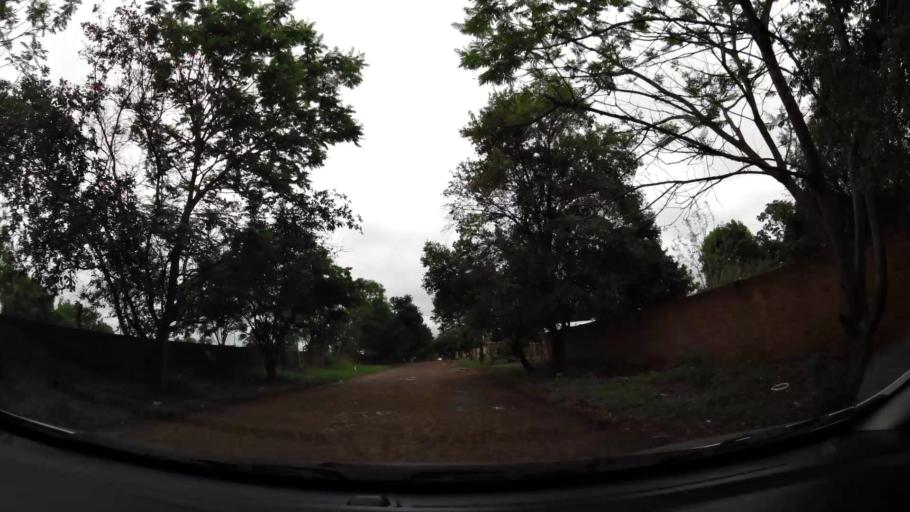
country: PY
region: Alto Parana
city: Presidente Franco
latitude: -25.4866
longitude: -54.7929
